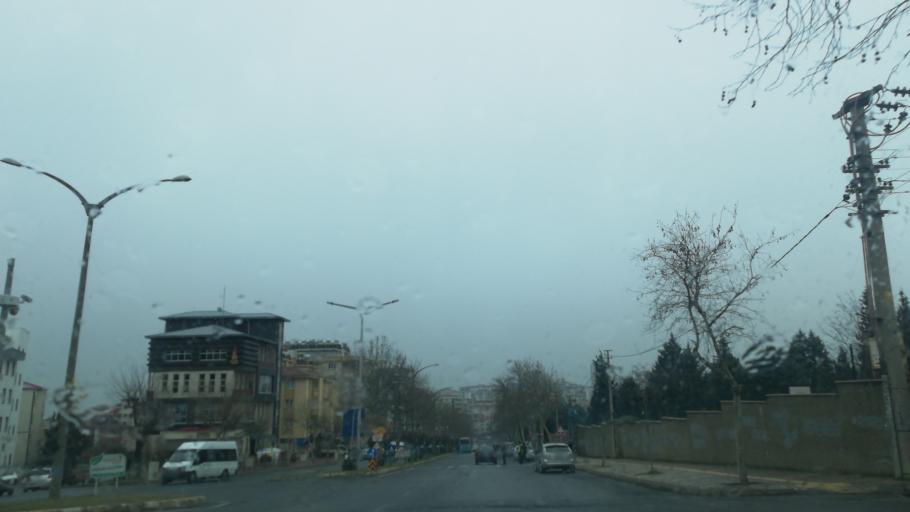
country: TR
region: Kahramanmaras
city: Kahramanmaras
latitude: 37.5902
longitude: 36.9025
